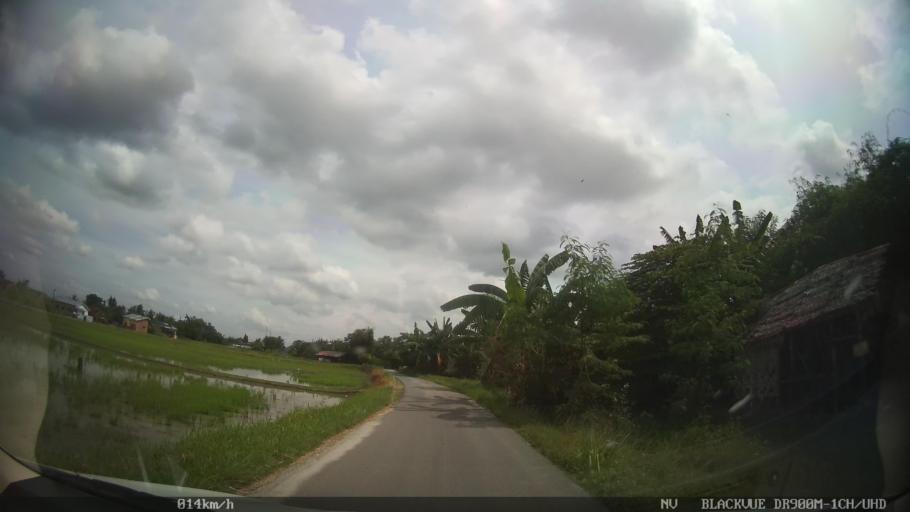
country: ID
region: North Sumatra
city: Percut
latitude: 3.5675
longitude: 98.8534
